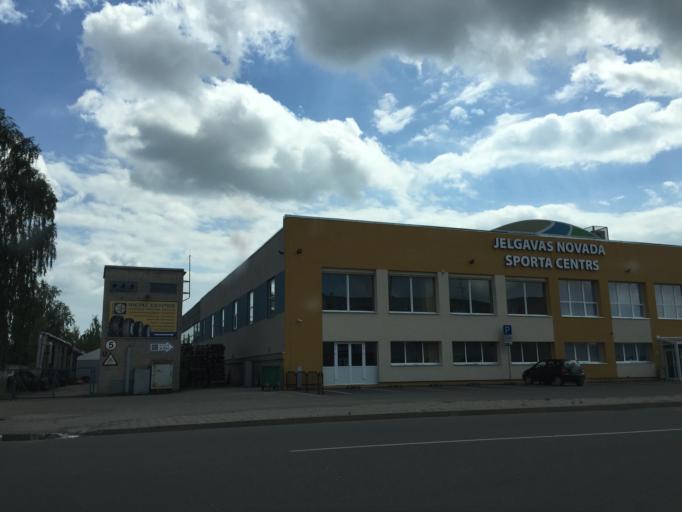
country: LV
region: Ozolnieku
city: Ozolnieki
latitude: 56.6559
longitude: 23.7582
